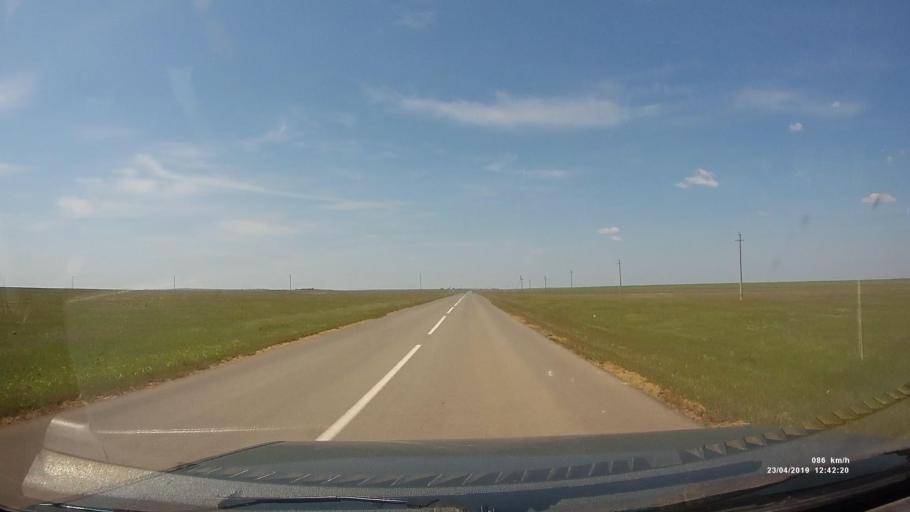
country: RU
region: Kalmykiya
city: Yashalta
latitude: 46.4551
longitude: 42.6672
